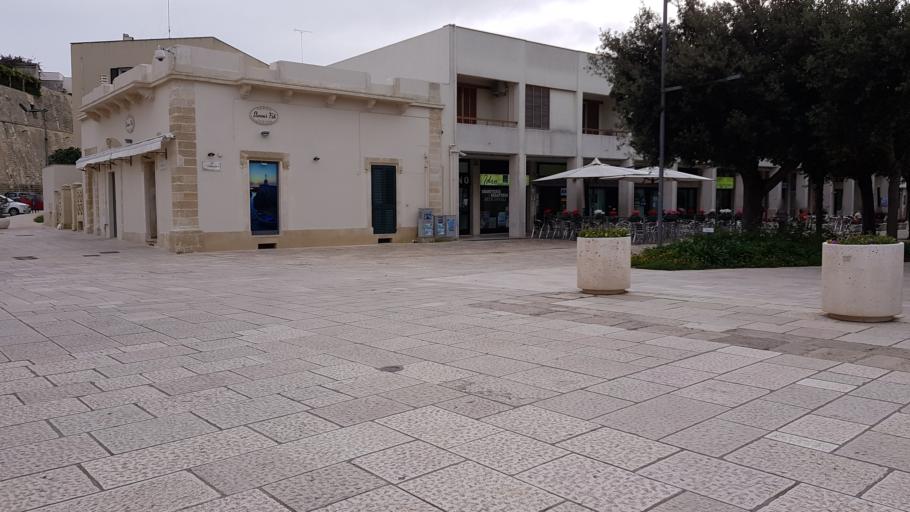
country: IT
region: Apulia
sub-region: Provincia di Lecce
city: Otranto
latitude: 40.1465
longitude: 18.4902
